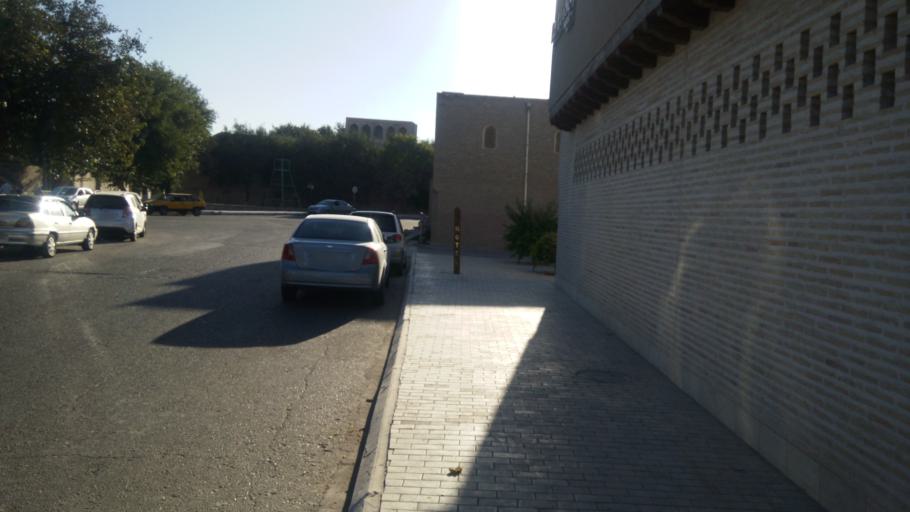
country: UZ
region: Bukhara
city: Bukhara
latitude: 39.7737
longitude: 64.4231
